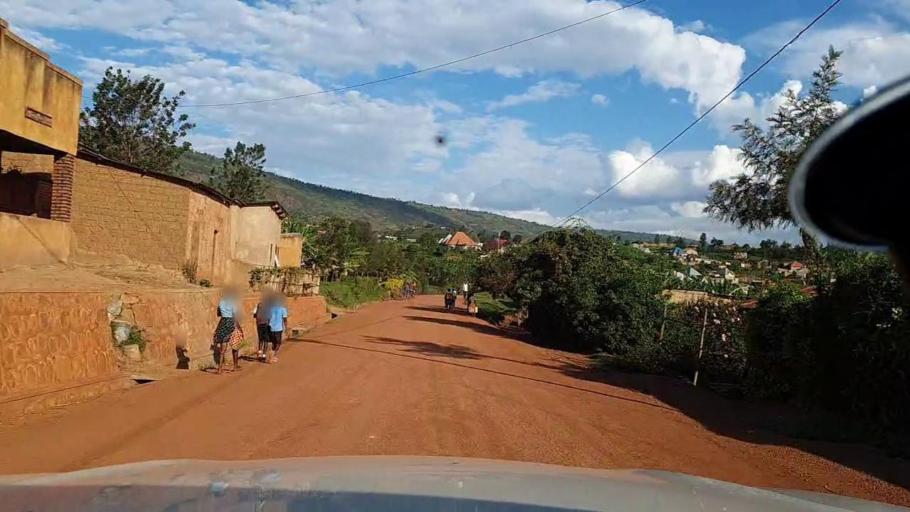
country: RW
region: Kigali
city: Kigali
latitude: -1.8941
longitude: 29.9623
